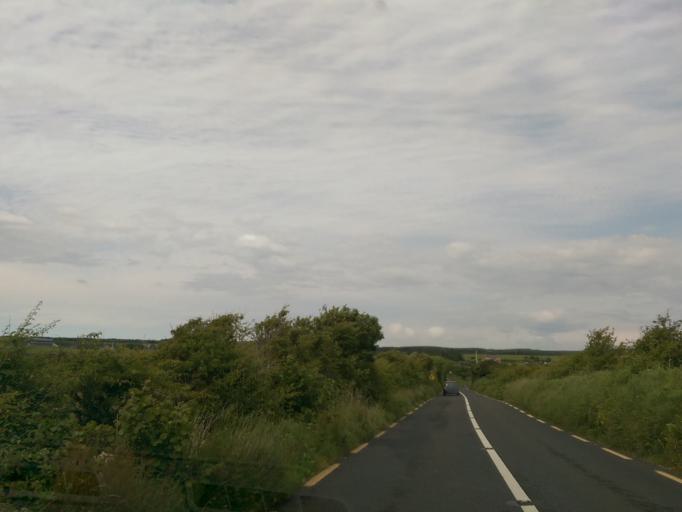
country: IE
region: Connaught
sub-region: County Galway
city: Bearna
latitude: 53.0226
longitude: -9.3081
